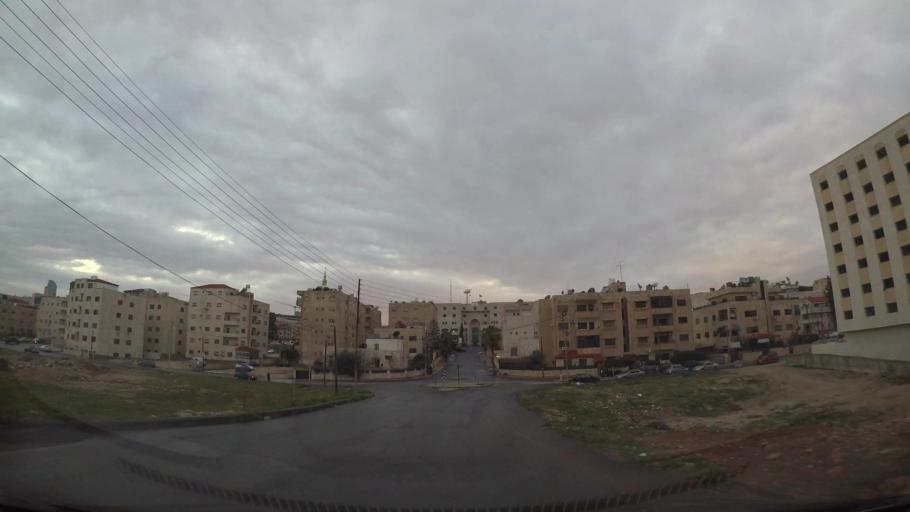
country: JO
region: Amman
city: Amman
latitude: 31.9801
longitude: 35.9127
